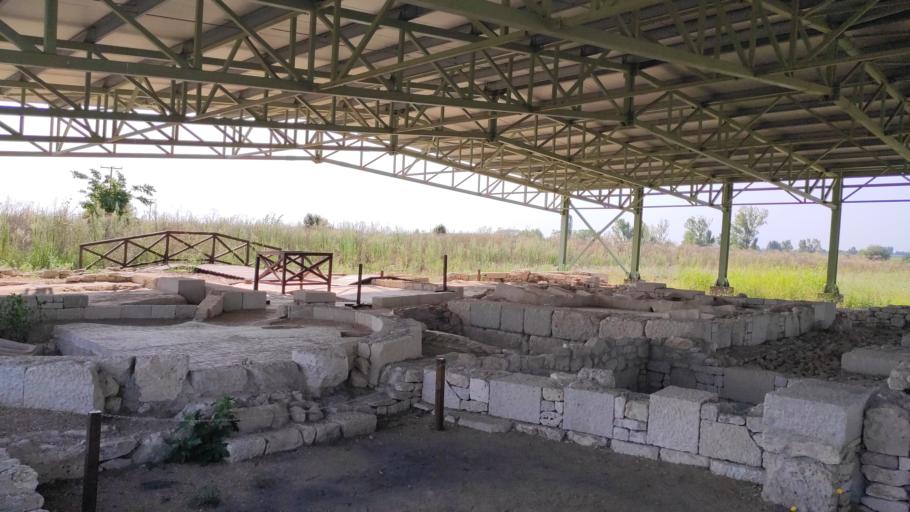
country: GR
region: Central Macedonia
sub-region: Nomos Pellis
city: Pella
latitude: 40.7523
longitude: 22.5183
